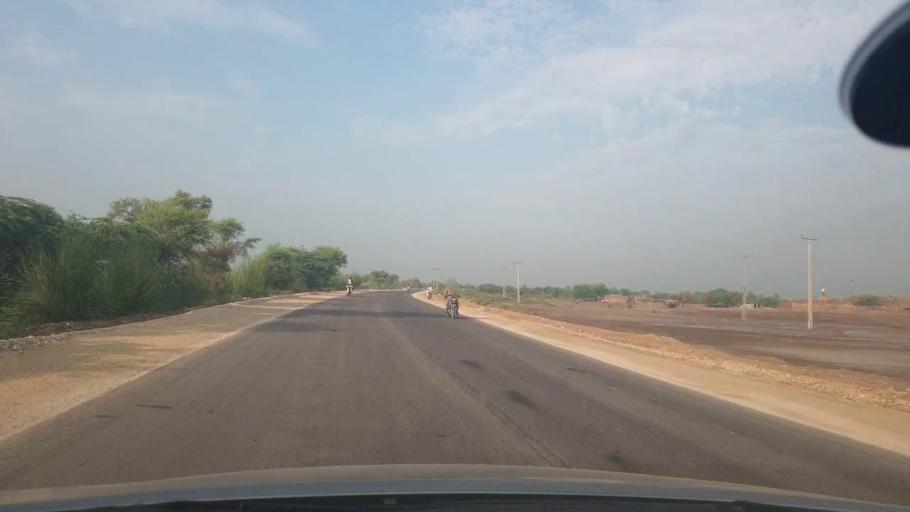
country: PK
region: Sindh
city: Jacobabad
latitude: 28.2464
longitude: 68.3997
